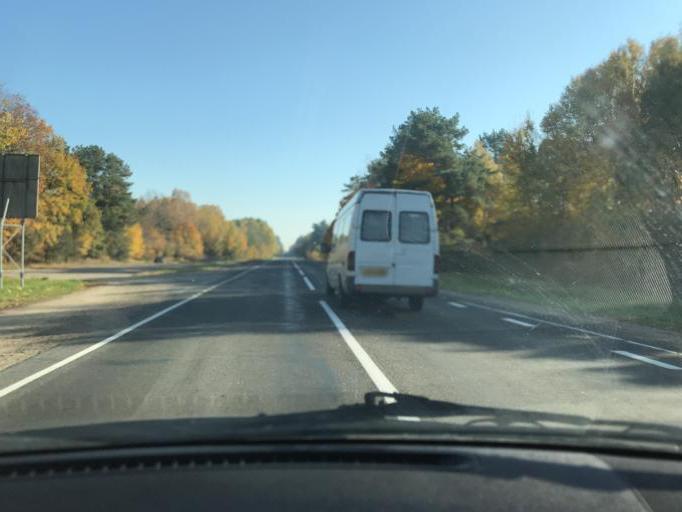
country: BY
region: Brest
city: Lyakhavichy
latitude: 52.9584
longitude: 26.3537
